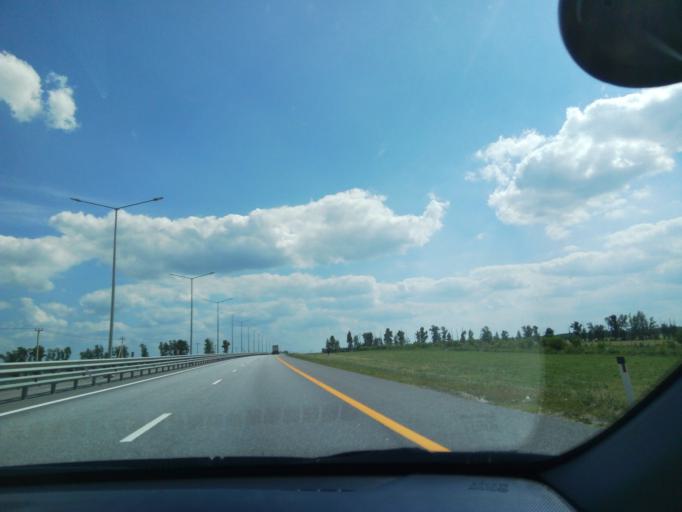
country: RU
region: Voronezj
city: Podkletnoye
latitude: 51.5281
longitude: 39.5096
